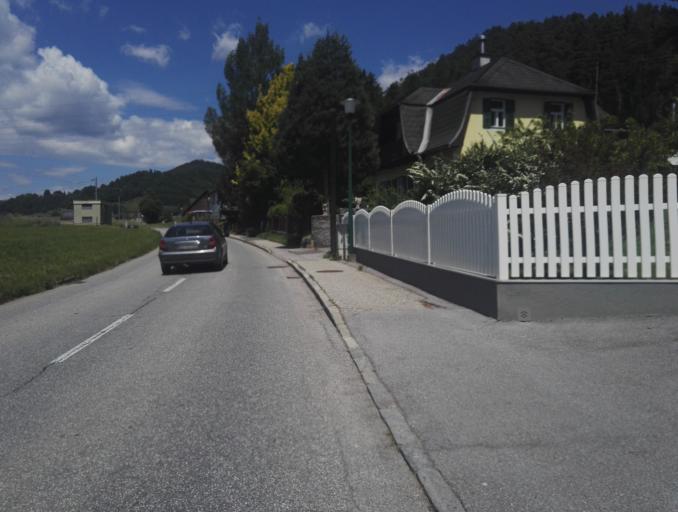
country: AT
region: Styria
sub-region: Politischer Bezirk Graz-Umgebung
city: Peggau
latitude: 47.2025
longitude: 15.3325
